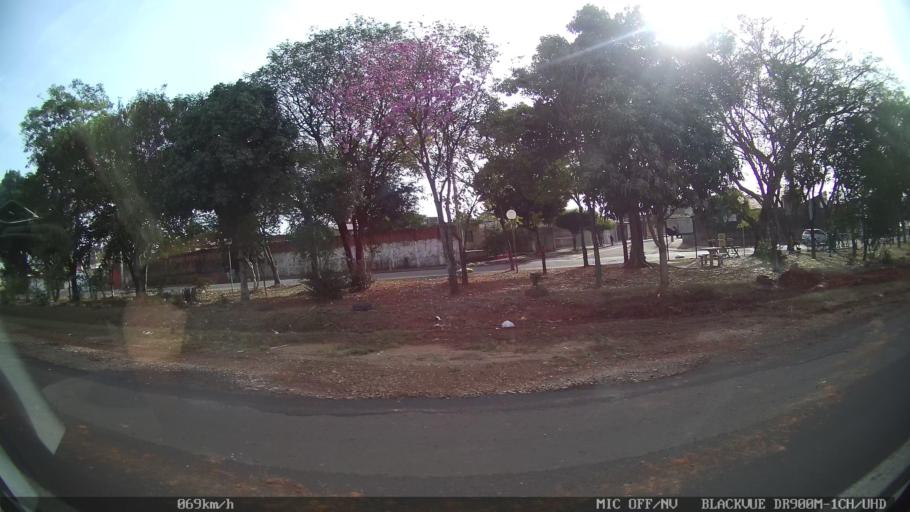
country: BR
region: Sao Paulo
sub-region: Piracicaba
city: Piracicaba
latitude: -22.6794
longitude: -47.7076
